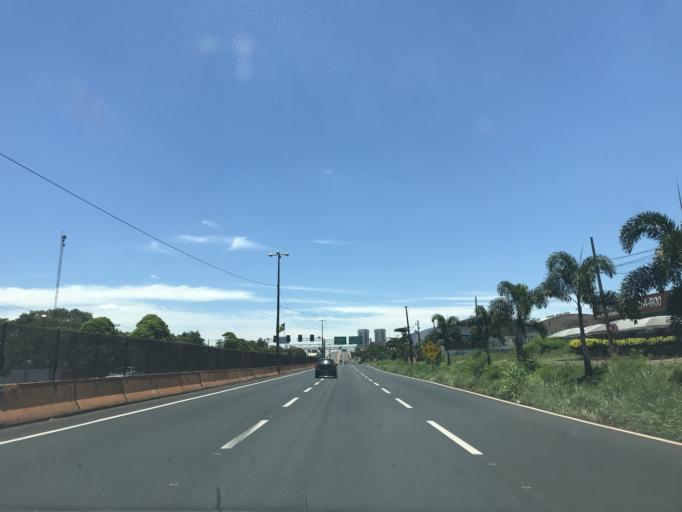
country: BR
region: Parana
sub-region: Sarandi
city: Sarandi
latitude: -23.4350
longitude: -51.8819
